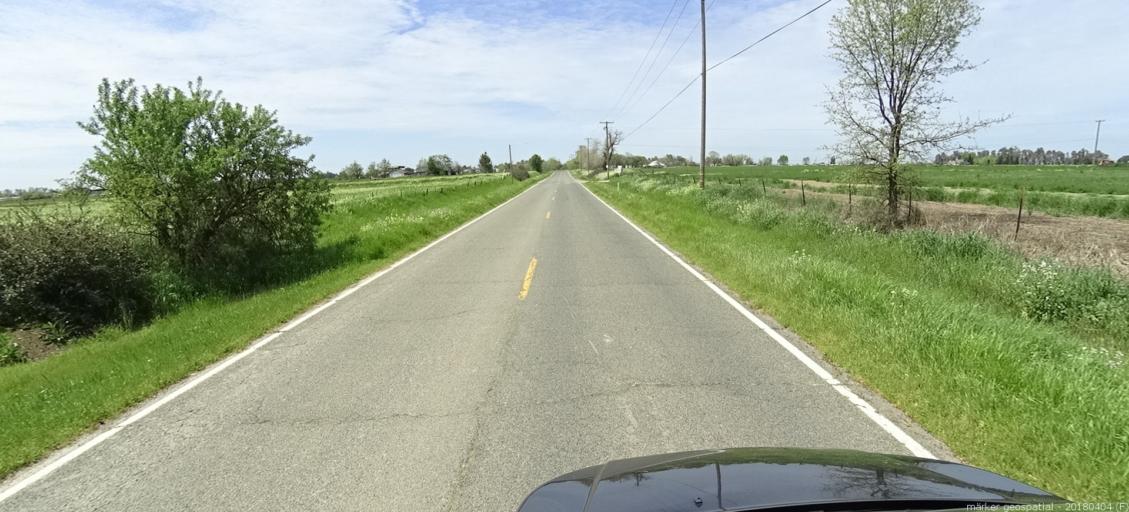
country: US
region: California
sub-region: Sacramento County
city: Herald
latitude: 38.2626
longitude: -121.2483
